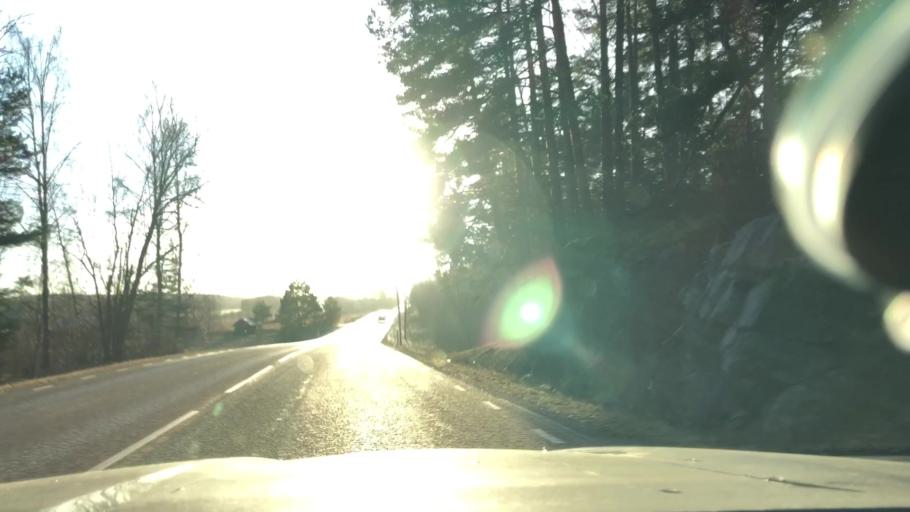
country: SE
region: Stockholm
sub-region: Sodertalje Kommun
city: Pershagen
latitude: 59.0418
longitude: 17.6036
